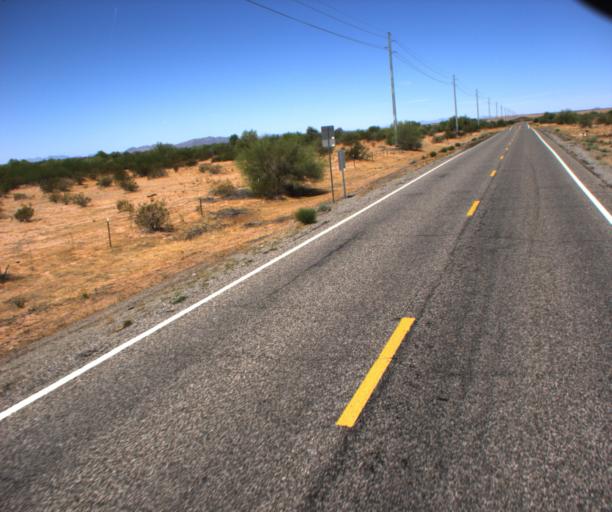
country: US
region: Arizona
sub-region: La Paz County
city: Cienega Springs
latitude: 33.9840
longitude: -114.0656
